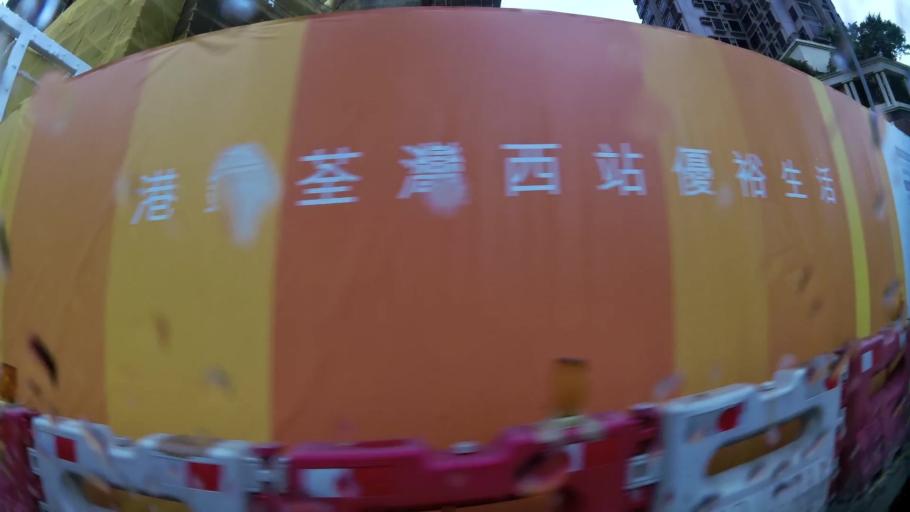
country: HK
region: Tsuen Wan
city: Tsuen Wan
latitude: 22.3691
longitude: 114.1122
